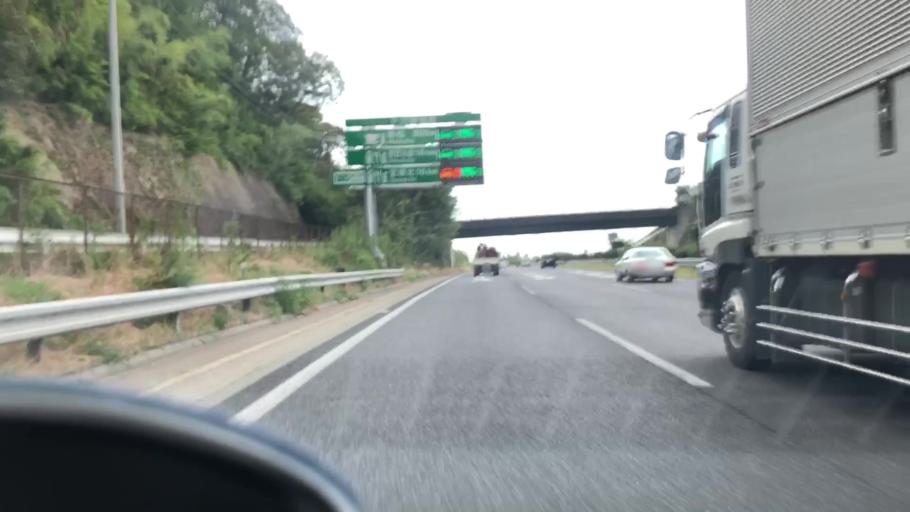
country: JP
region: Hyogo
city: Sandacho
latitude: 34.8896
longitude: 135.1603
